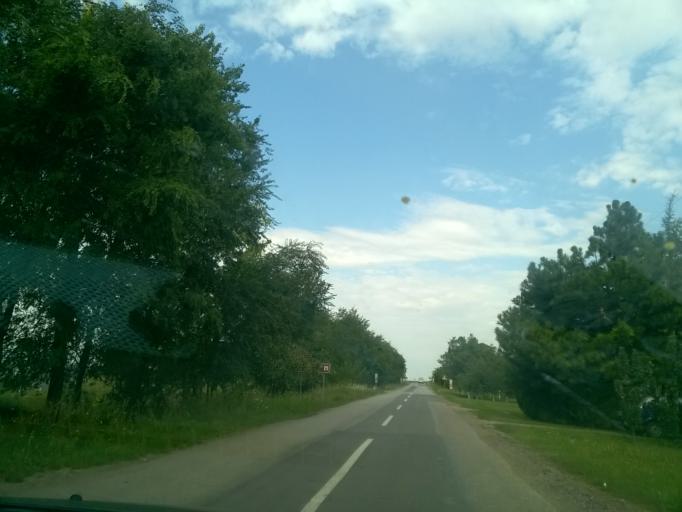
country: RS
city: Orlovat
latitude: 45.2495
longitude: 20.5787
